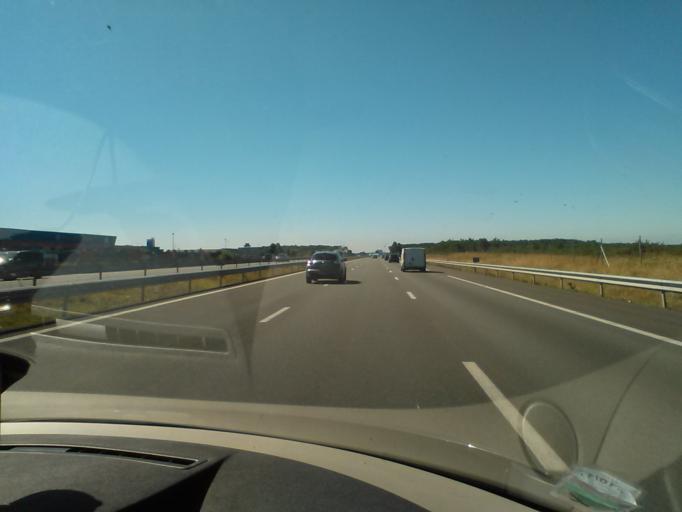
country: FR
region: Aquitaine
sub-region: Departement des Landes
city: Saint-Geours-de-Maremne
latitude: 43.7229
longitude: -1.2275
